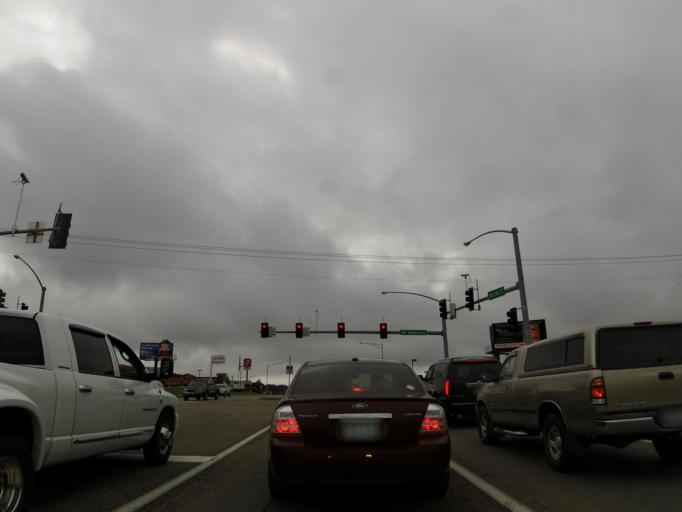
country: US
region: Missouri
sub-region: Cape Girardeau County
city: Cape Girardeau
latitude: 37.3020
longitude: -89.5749
